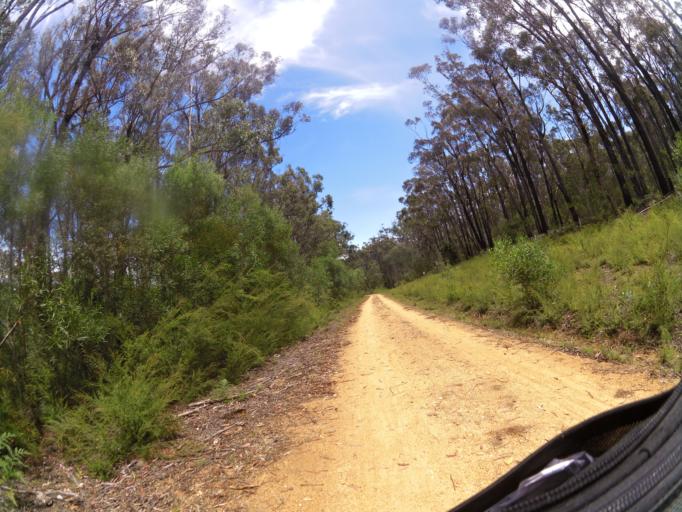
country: AU
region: Victoria
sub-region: East Gippsland
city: Lakes Entrance
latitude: -37.7436
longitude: 148.0003
